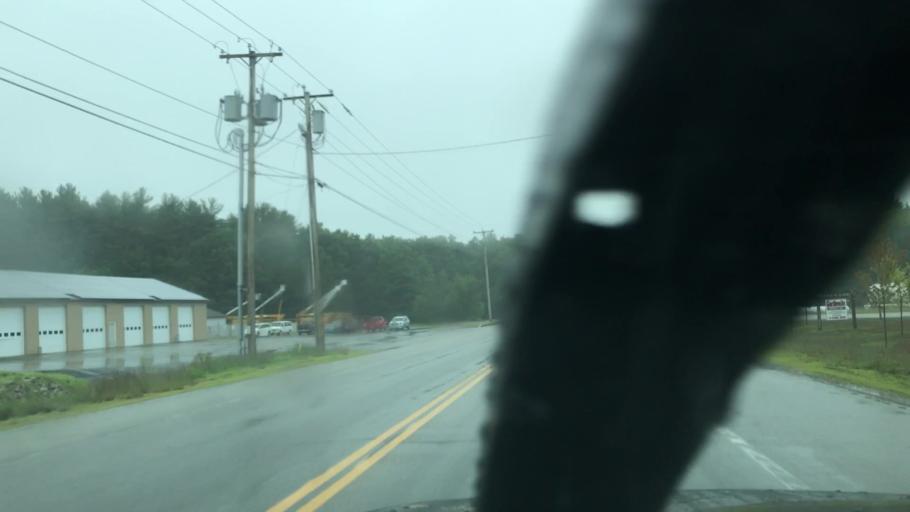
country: US
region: Maine
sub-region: York County
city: Wells Beach Station
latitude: 43.3208
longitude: -70.6460
